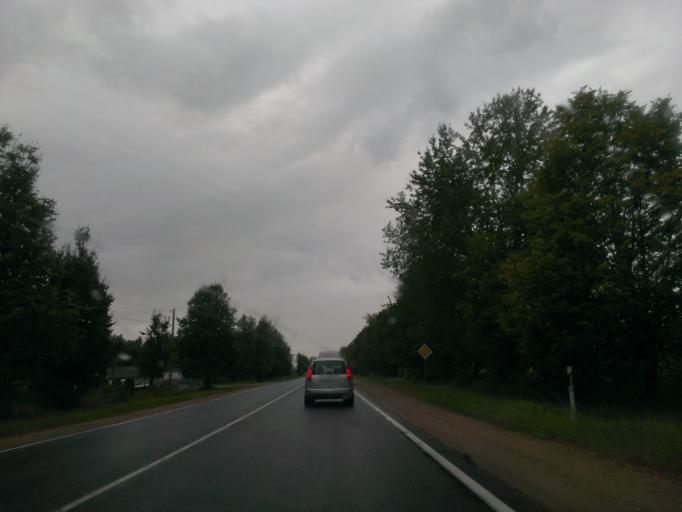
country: LV
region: Ogre
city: Ogre
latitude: 56.7812
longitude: 24.6508
